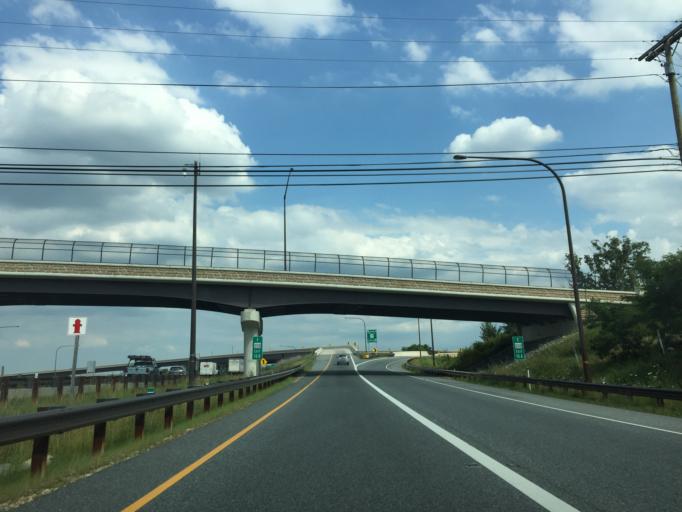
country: US
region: Maryland
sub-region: Montgomery County
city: Fairland
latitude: 39.0796
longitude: -76.9565
